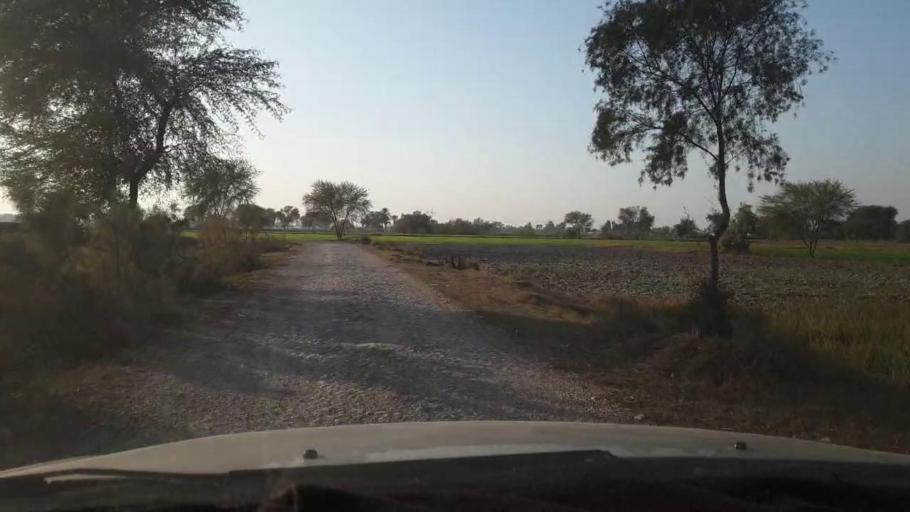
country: PK
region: Sindh
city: Mirpur Mathelo
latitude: 28.0007
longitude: 69.5065
